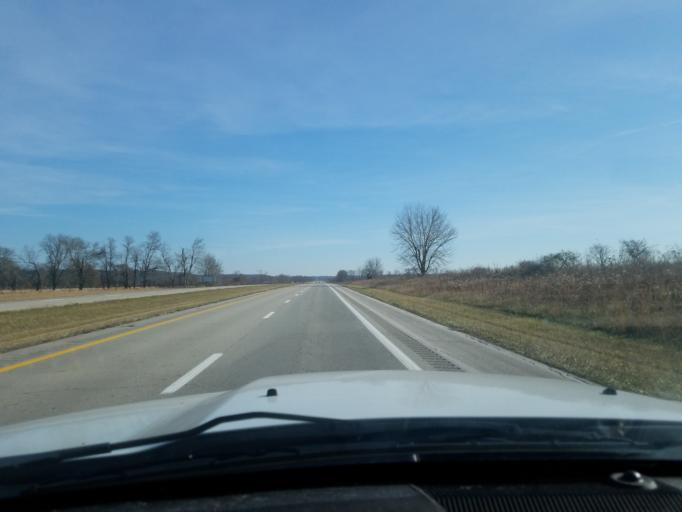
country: US
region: Ohio
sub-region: Jackson County
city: Jackson
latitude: 39.0120
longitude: -82.8126
